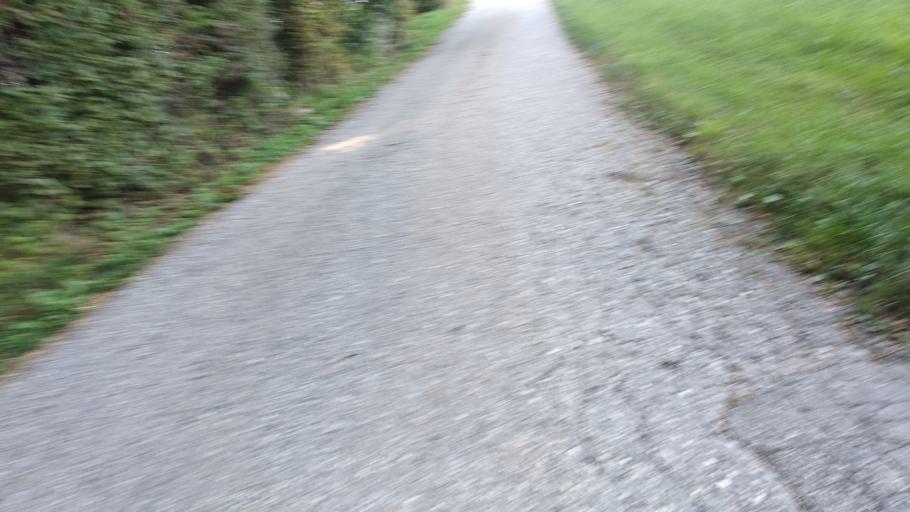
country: DE
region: Bavaria
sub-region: Upper Bavaria
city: Isen
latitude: 48.2001
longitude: 12.0687
